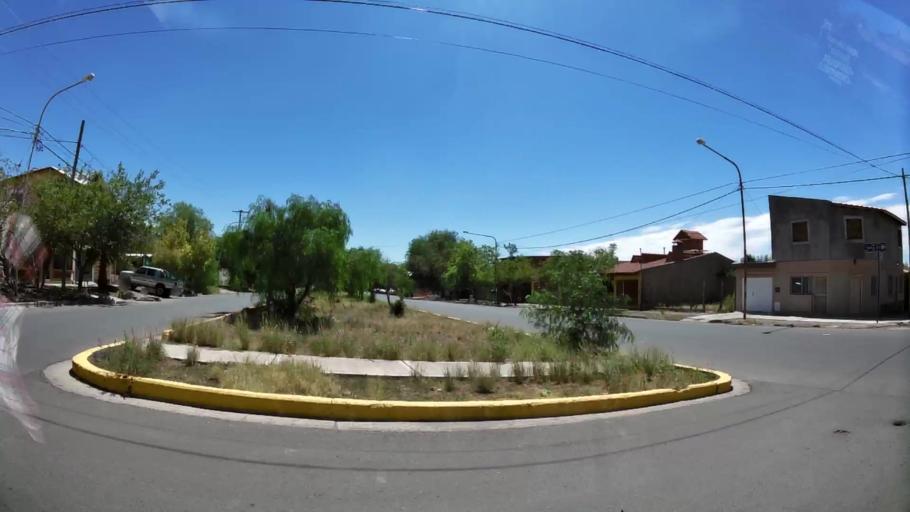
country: AR
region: Mendoza
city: Las Heras
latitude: -32.8470
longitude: -68.8728
